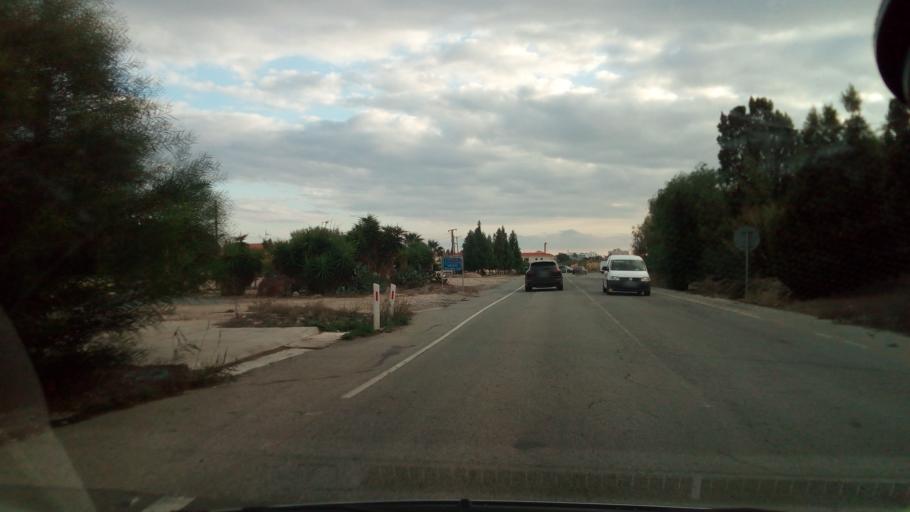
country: CY
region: Larnaka
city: Voroklini
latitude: 34.9721
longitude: 33.6574
